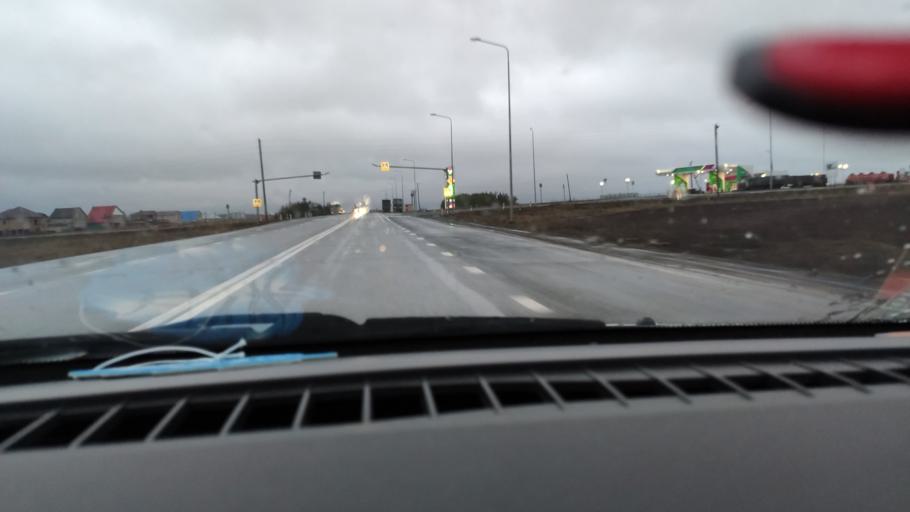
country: RU
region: Udmurtiya
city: Alnashi
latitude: 56.1720
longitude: 52.4738
